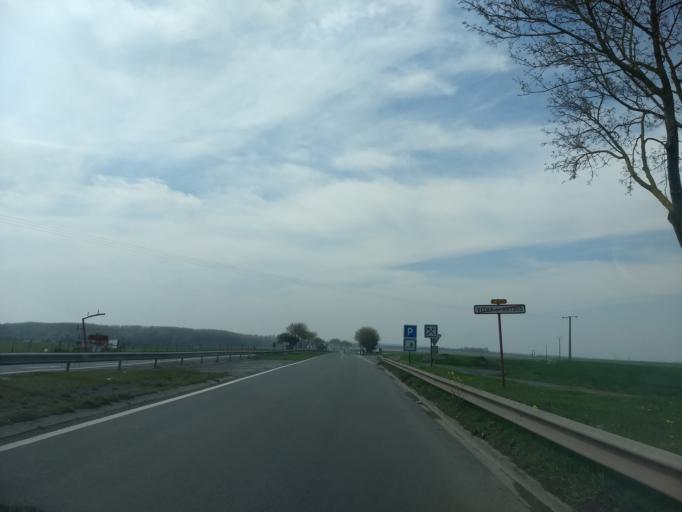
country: FR
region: Nord-Pas-de-Calais
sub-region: Departement du Pas-de-Calais
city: Vitry-en-Artois
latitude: 50.3327
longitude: 2.9721
